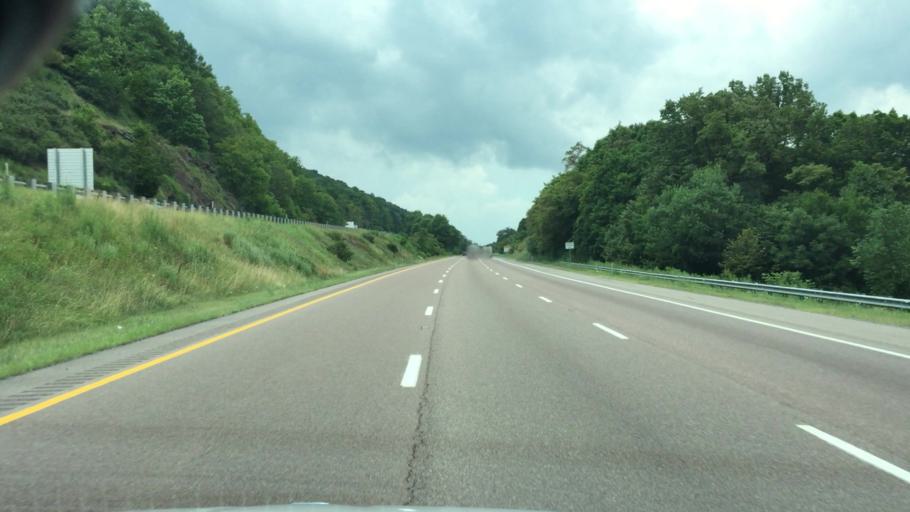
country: US
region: Maryland
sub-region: Allegany County
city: La Vale
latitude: 39.6369
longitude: -78.8526
